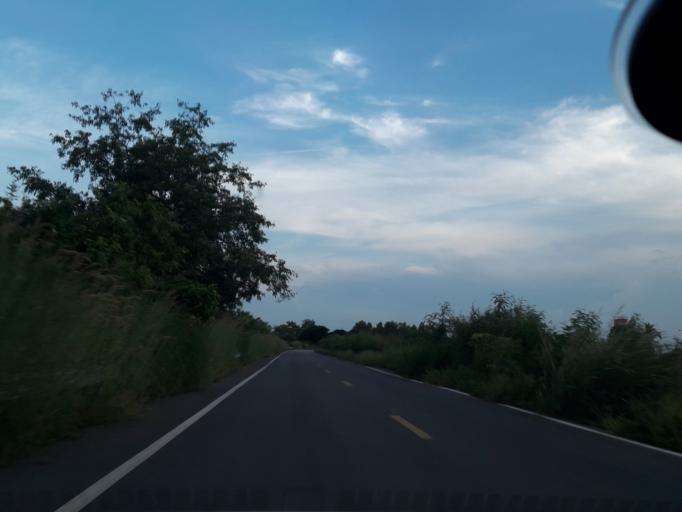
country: TH
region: Sara Buri
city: Nong Khae
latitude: 14.3020
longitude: 100.8895
